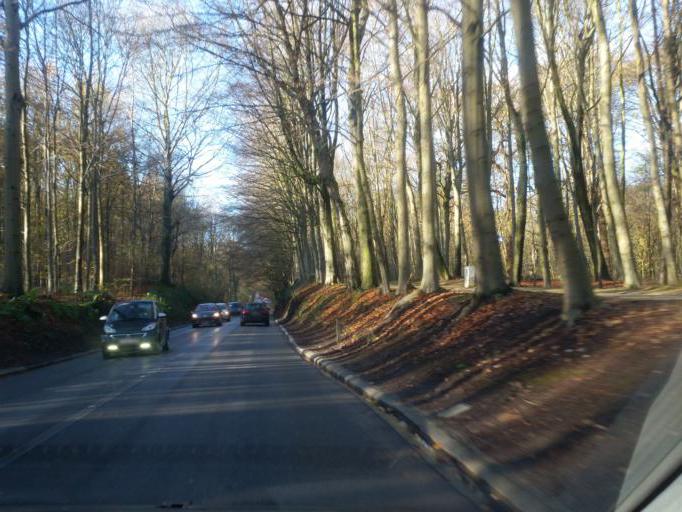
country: BE
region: Flanders
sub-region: Provincie Vlaams-Brabant
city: Sint-Genesius-Rode
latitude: 50.7978
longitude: 4.3896
